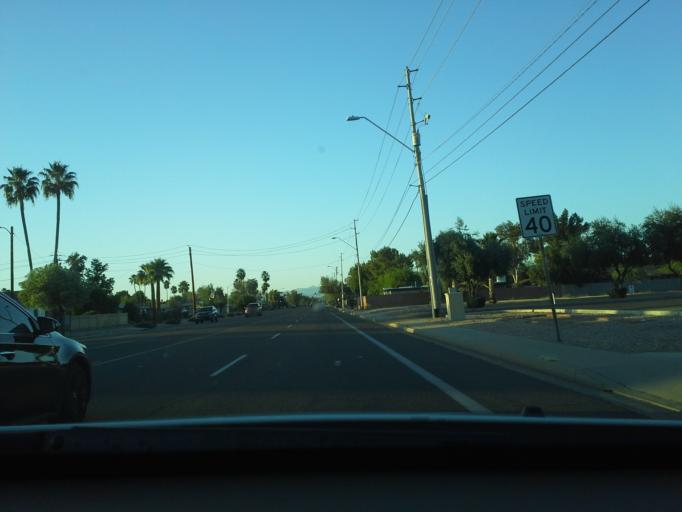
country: US
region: Arizona
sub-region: Maricopa County
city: Paradise Valley
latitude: 33.5873
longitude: -111.9957
